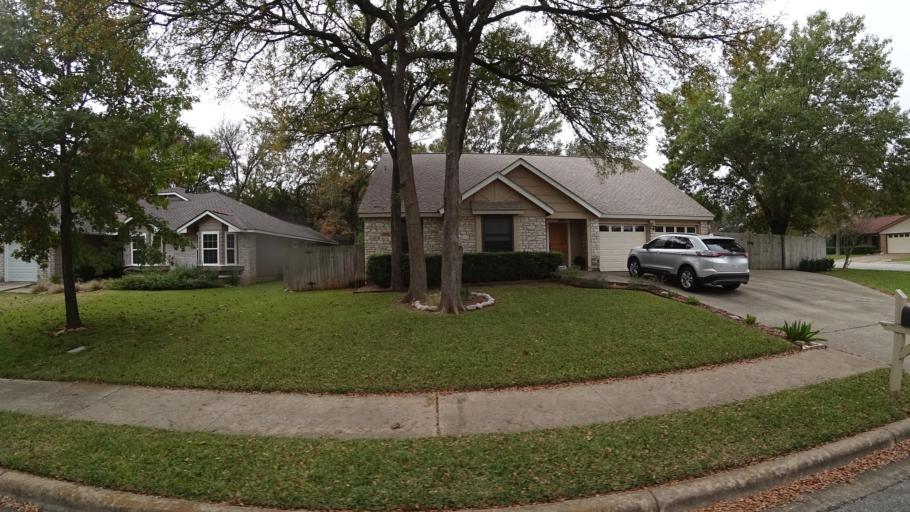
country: US
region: Texas
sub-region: Travis County
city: Wells Branch
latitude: 30.4336
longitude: -97.7173
